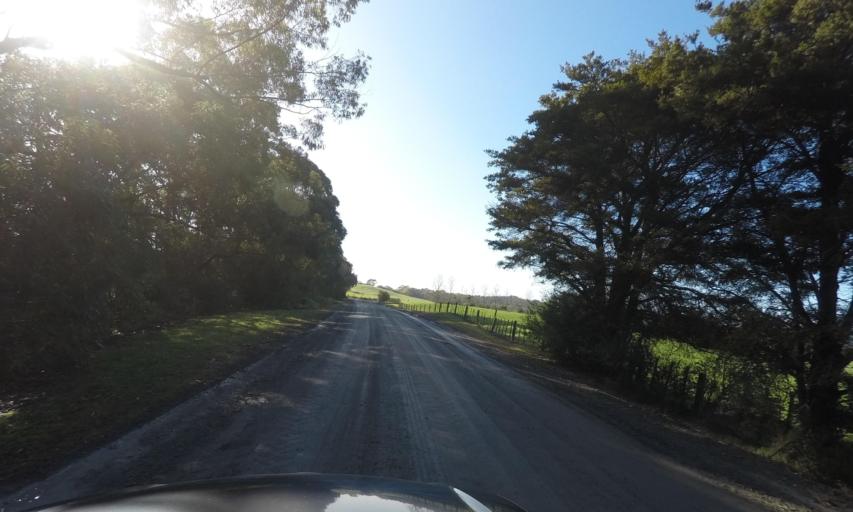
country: NZ
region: Auckland
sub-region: Auckland
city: Wellsford
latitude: -36.1463
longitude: 174.6027
